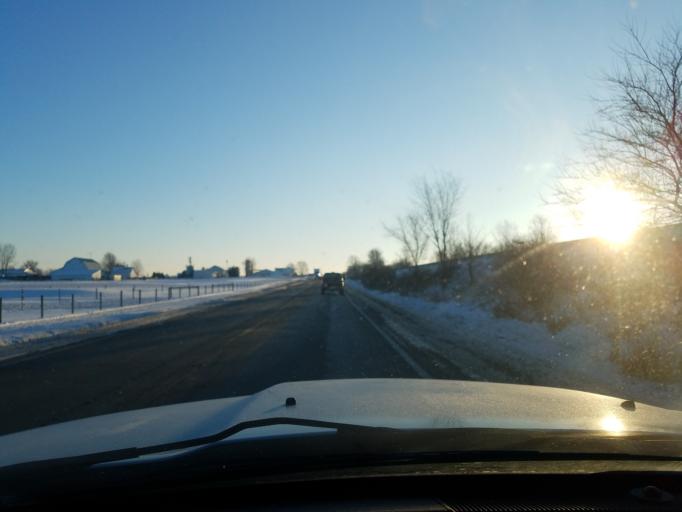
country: US
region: Indiana
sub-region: Elkhart County
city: Nappanee
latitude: 41.4447
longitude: -86.0491
